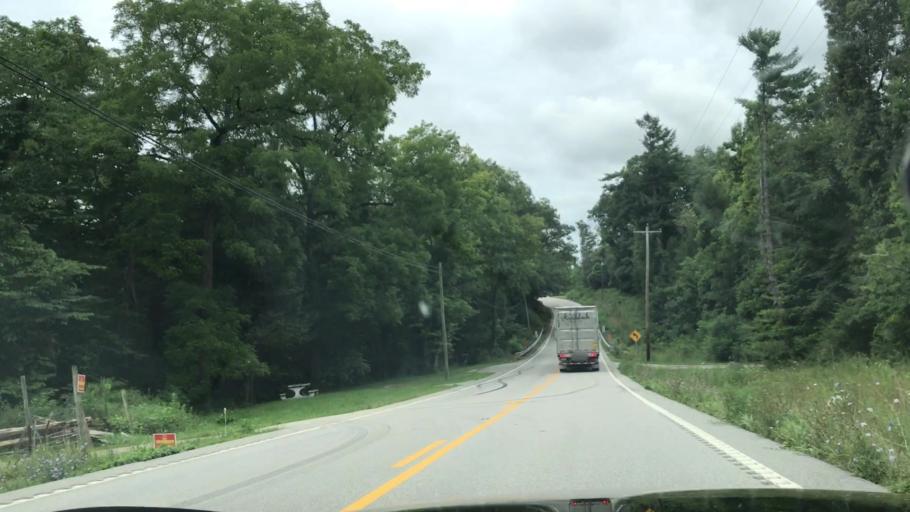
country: US
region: Tennessee
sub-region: Fentress County
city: Jamestown
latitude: 36.3744
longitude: -84.7764
